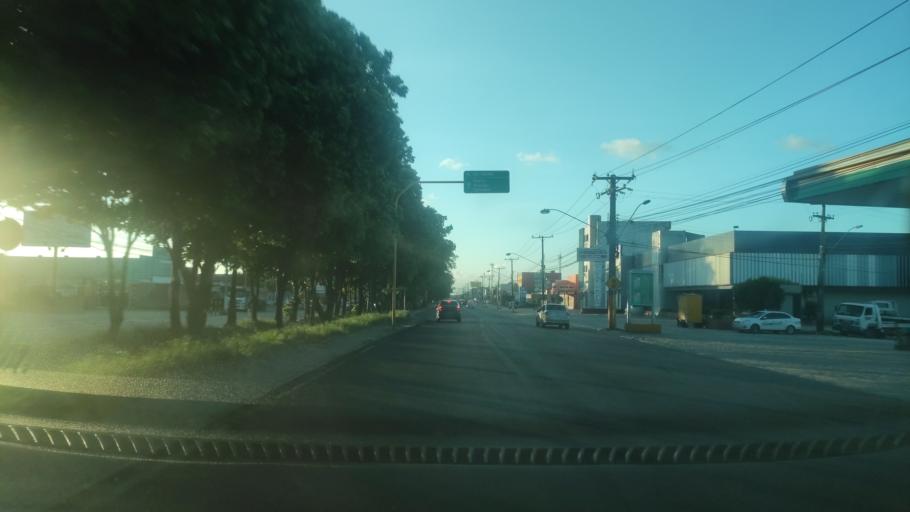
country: BR
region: Alagoas
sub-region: Satuba
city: Satuba
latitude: -9.5885
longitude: -35.7614
